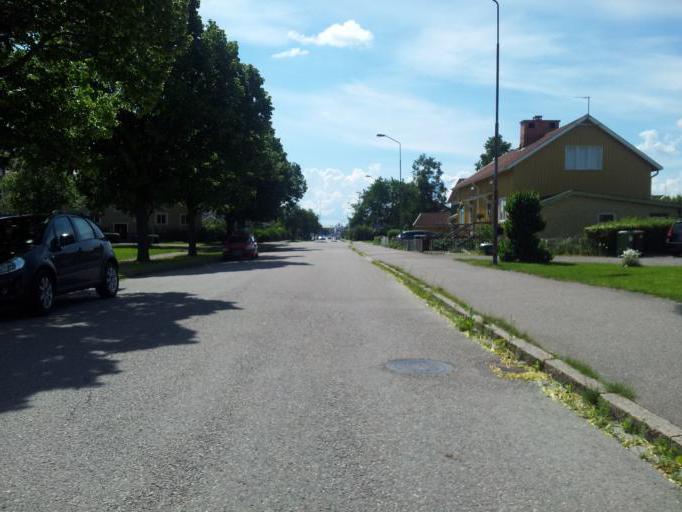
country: SE
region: Uppsala
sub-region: Uppsala Kommun
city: Uppsala
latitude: 59.8609
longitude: 17.6648
